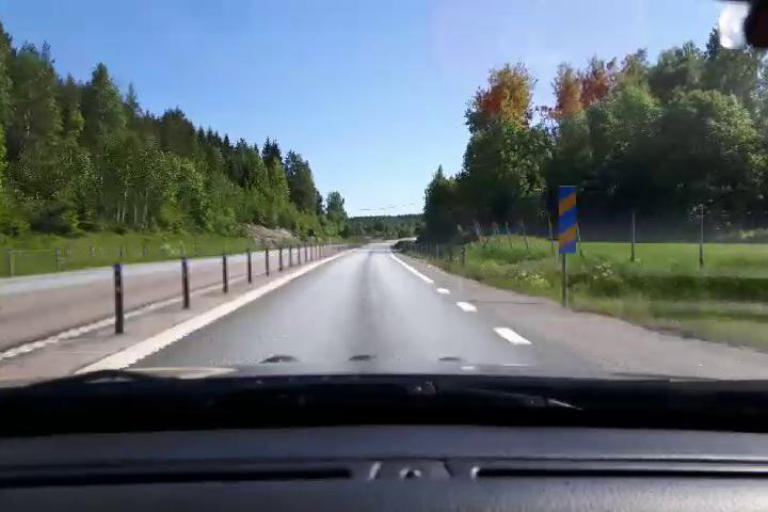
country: SE
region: Gaevleborg
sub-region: Soderhamns Kommun
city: Soderhamn
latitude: 61.2832
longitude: 17.0263
